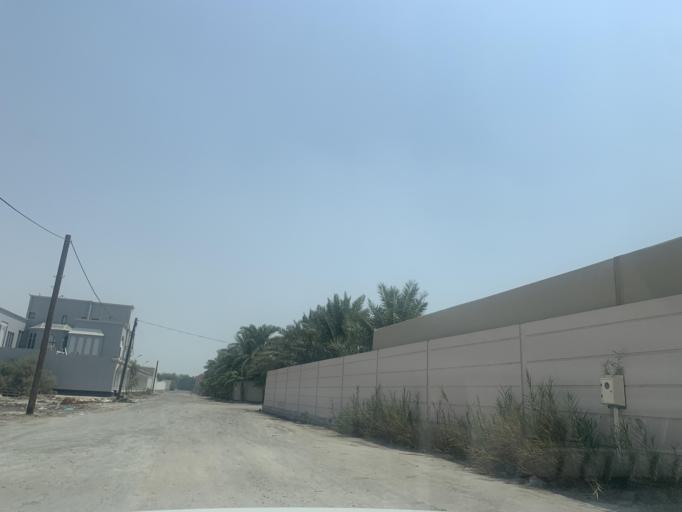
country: BH
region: Central Governorate
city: Madinat Hamad
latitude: 26.1270
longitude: 50.4679
